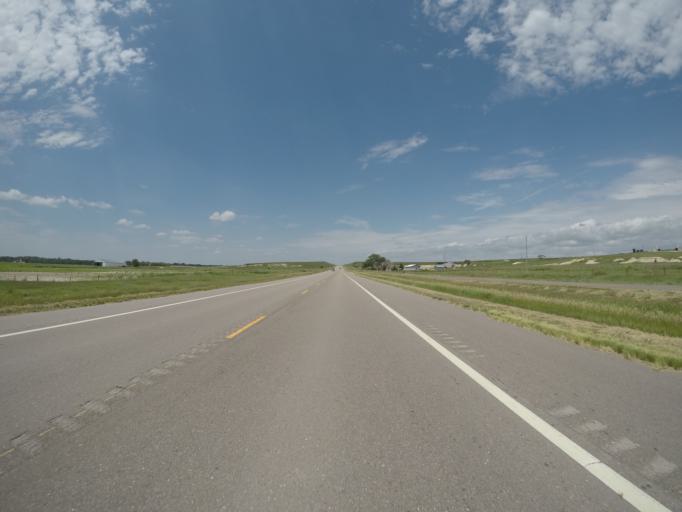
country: US
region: Kansas
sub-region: Graham County
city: Hill City
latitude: 39.3795
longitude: -99.6935
